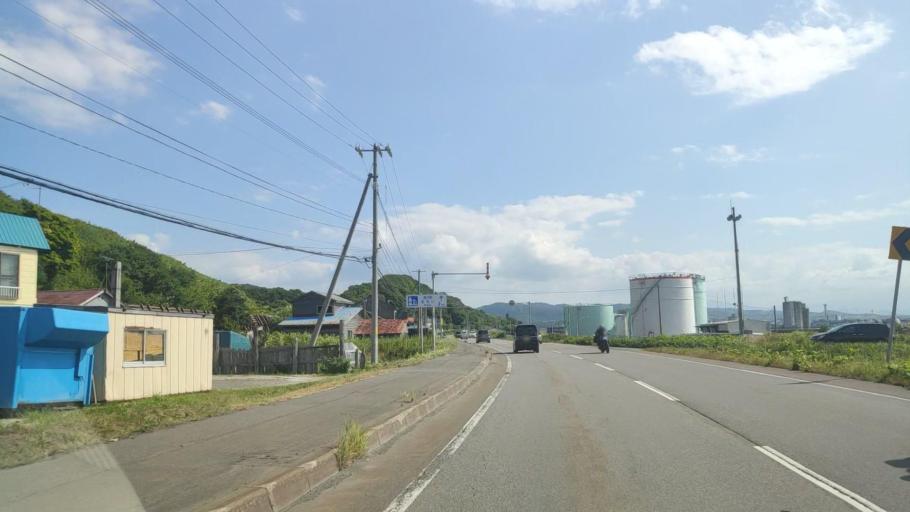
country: JP
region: Hokkaido
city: Rumoi
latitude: 43.9609
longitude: 141.6429
